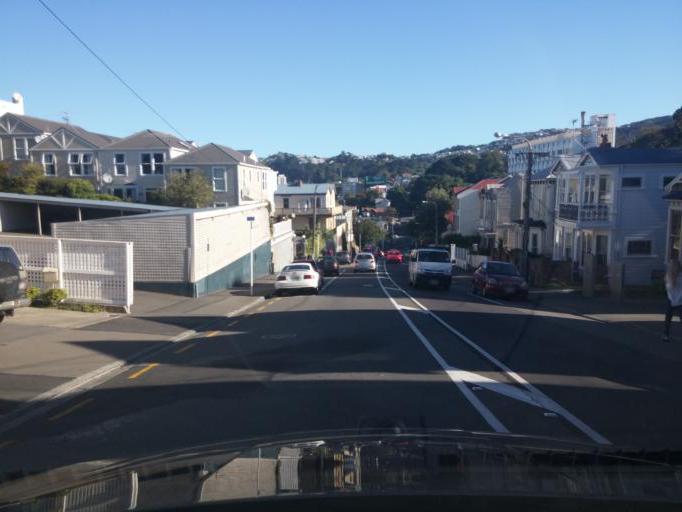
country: NZ
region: Wellington
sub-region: Wellington City
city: Wellington
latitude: -41.2894
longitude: 174.7718
